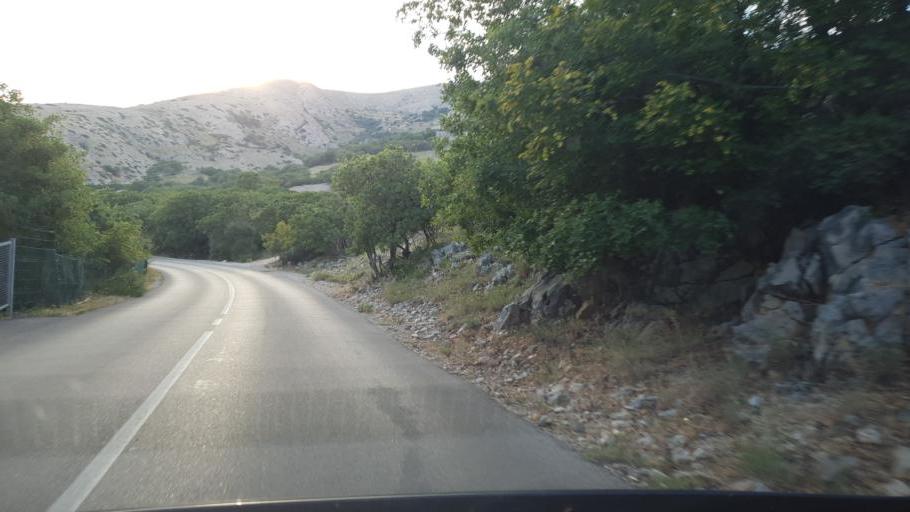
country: HR
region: Primorsko-Goranska
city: Punat
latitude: 44.9666
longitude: 14.6770
